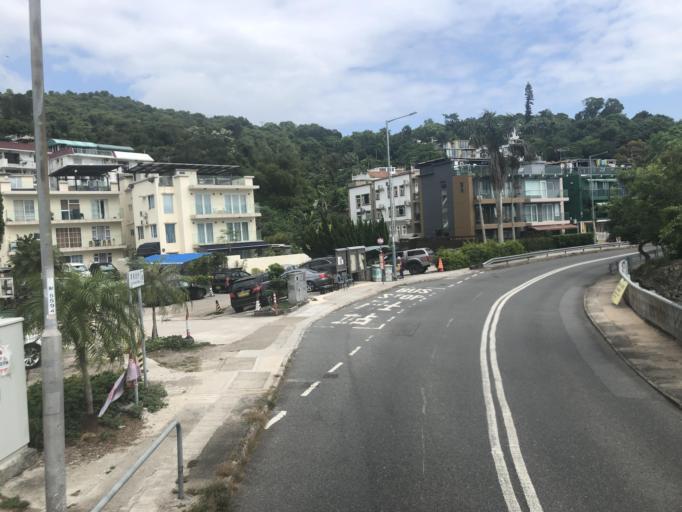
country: HK
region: Sai Kung
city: Sai Kung
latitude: 22.3942
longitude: 114.2888
